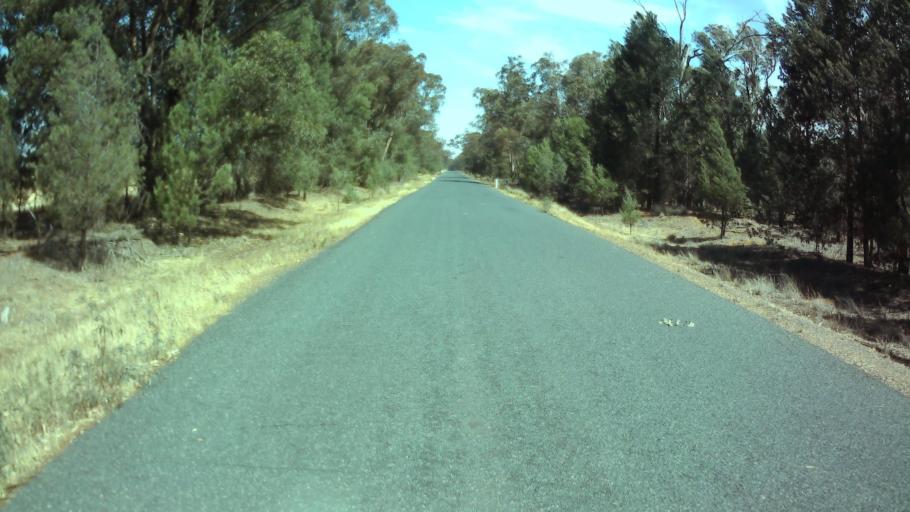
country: AU
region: New South Wales
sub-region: Weddin
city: Grenfell
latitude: -34.0601
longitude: 148.1325
